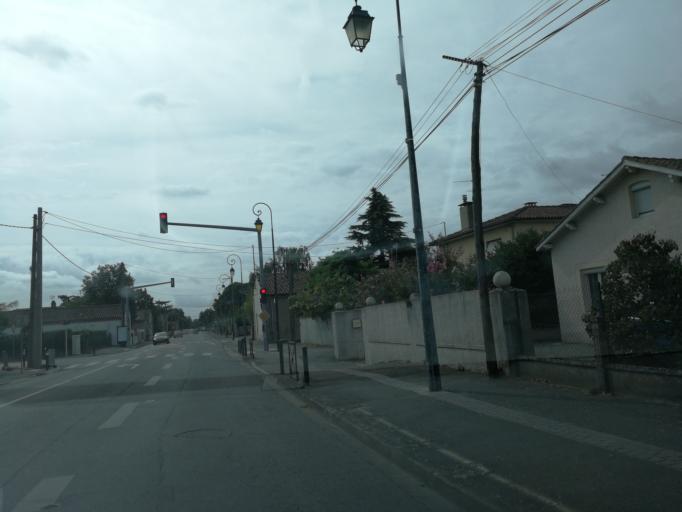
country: FR
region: Midi-Pyrenees
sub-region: Departement de la Haute-Garonne
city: Aucamville
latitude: 43.6742
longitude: 1.4253
